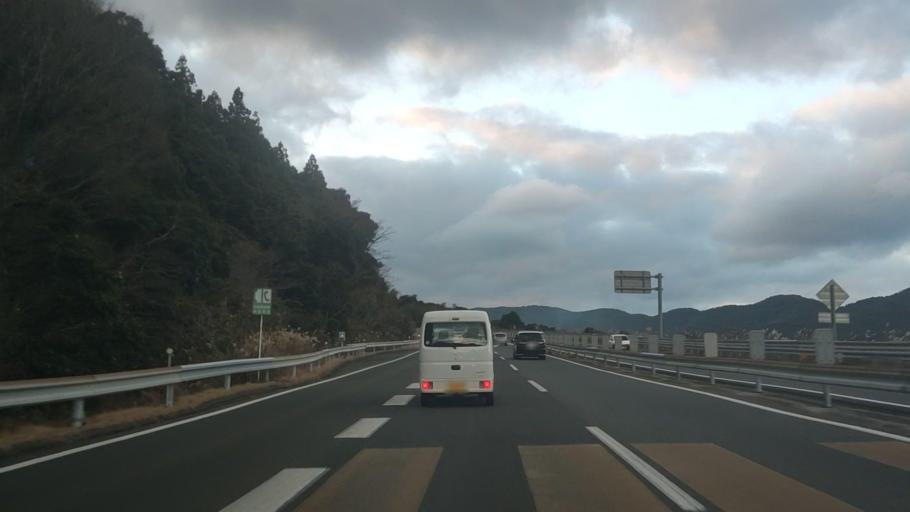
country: JP
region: Nagasaki
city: Obita
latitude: 32.8172
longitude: 129.9558
